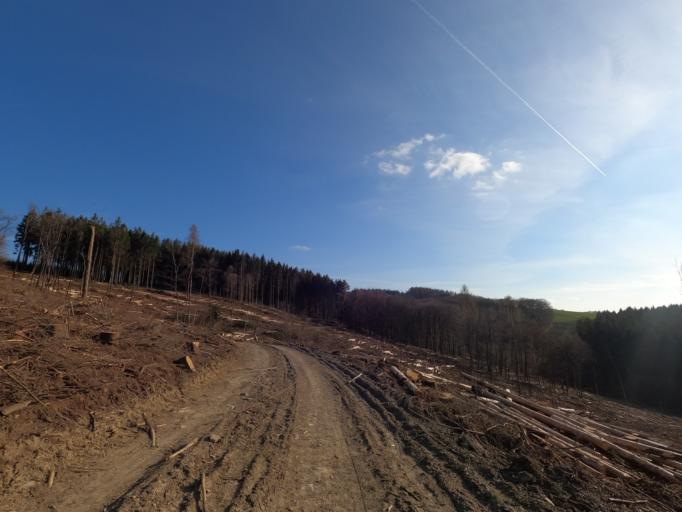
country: DE
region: North Rhine-Westphalia
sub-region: Regierungsbezirk Arnsberg
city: Herscheid
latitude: 51.1722
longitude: 7.7195
